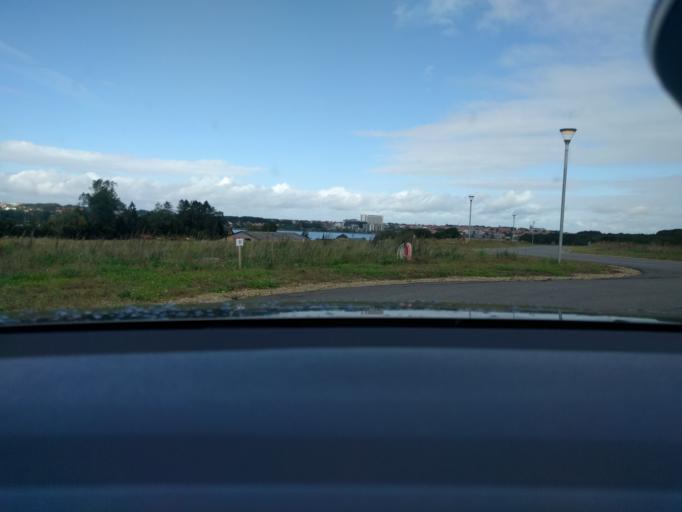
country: DK
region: Central Jutland
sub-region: Viborg Kommune
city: Viborg
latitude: 56.4304
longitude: 9.4209
